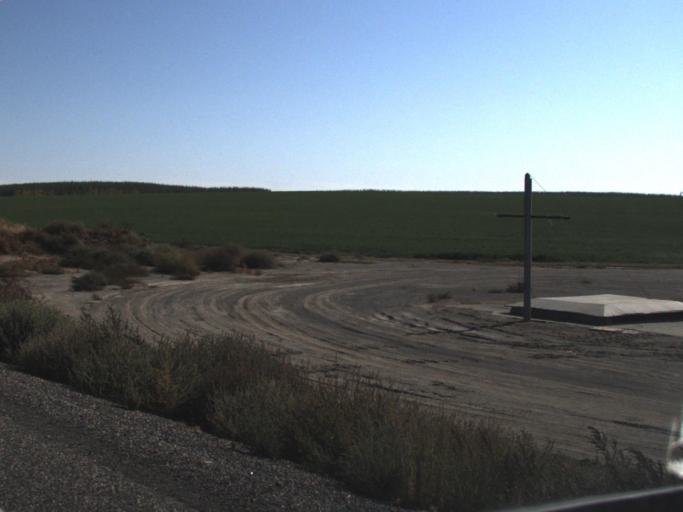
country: US
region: Washington
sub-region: Walla Walla County
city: Burbank
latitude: 46.2153
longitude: -118.9185
